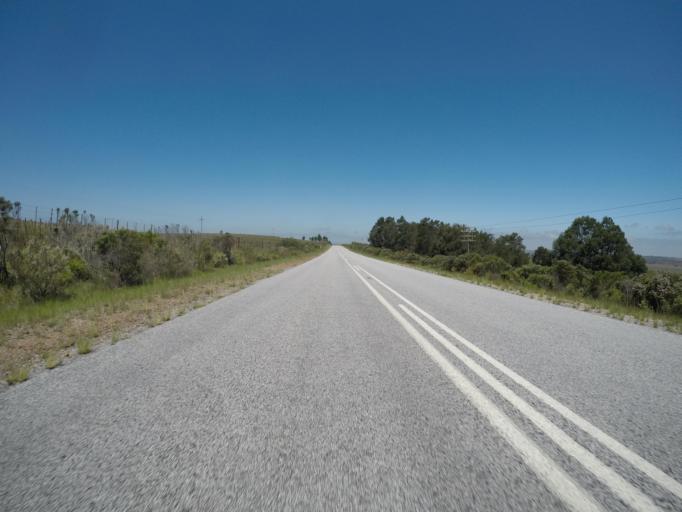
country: ZA
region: Eastern Cape
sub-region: Cacadu District Municipality
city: Kruisfontein
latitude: -33.9929
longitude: 24.5334
